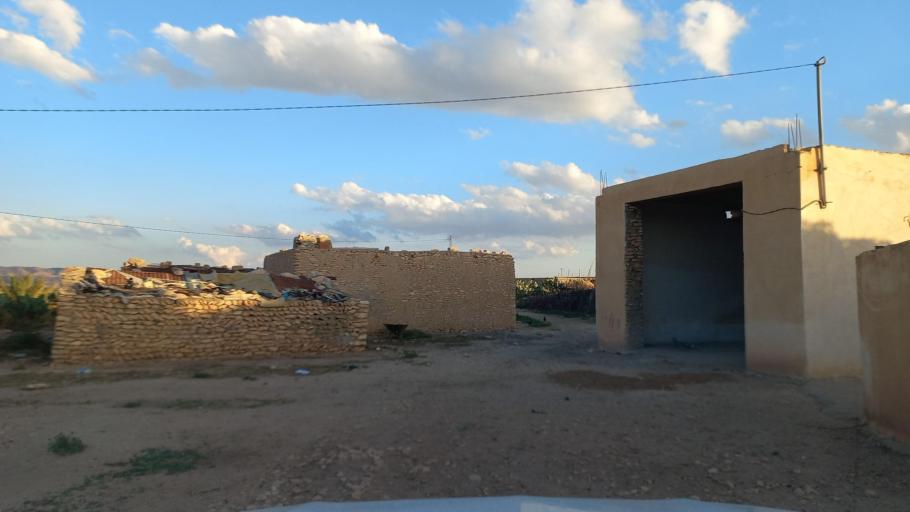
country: TN
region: Al Qasrayn
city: Sbiba
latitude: 35.3767
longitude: 9.0488
